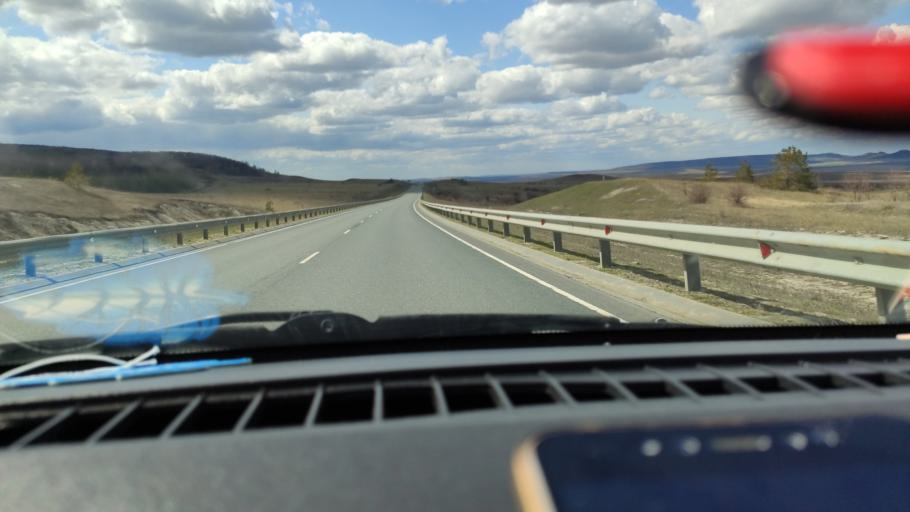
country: RU
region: Saratov
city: Alekseyevka
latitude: 52.3629
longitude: 47.9566
